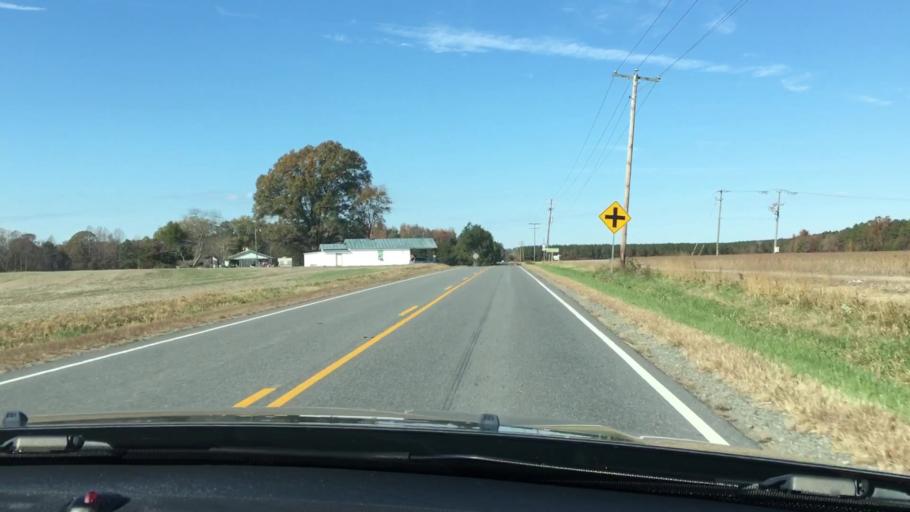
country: US
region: Virginia
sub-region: King and Queen County
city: King and Queen Court House
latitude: 37.6315
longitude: -76.9336
